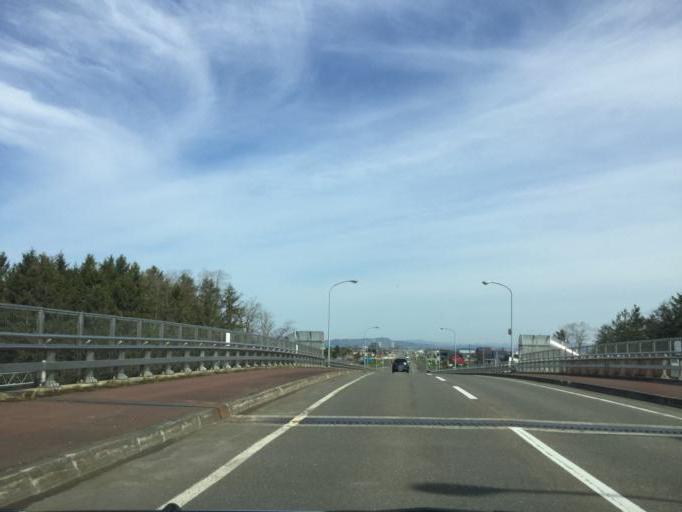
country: JP
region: Hokkaido
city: Iwamizawa
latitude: 43.1774
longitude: 141.7073
